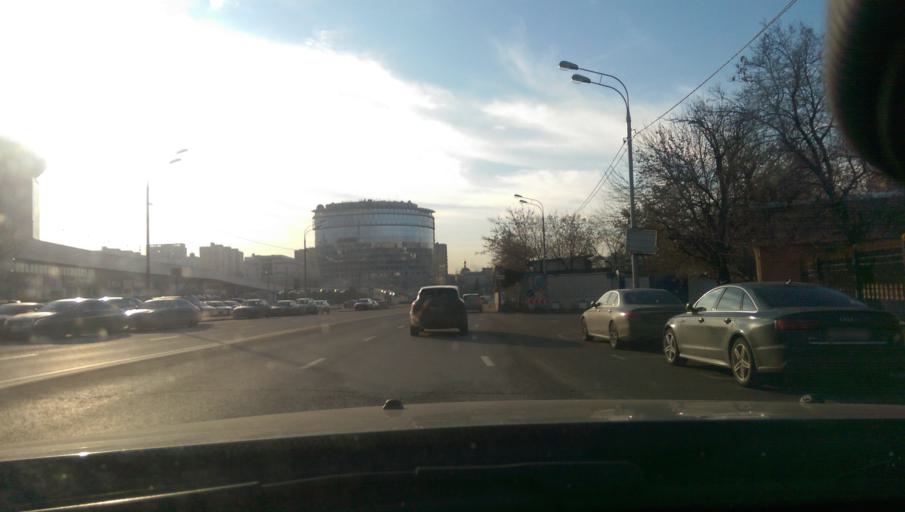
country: RU
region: Moscow
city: Mar'ina Roshcha
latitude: 55.7824
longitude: 37.6237
